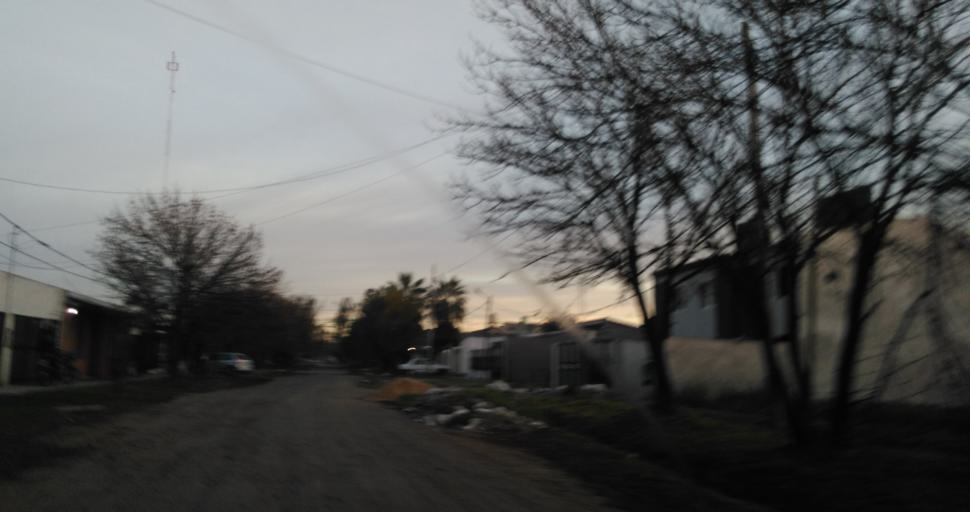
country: AR
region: Chaco
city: Resistencia
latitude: -27.4620
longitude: -59.0078
